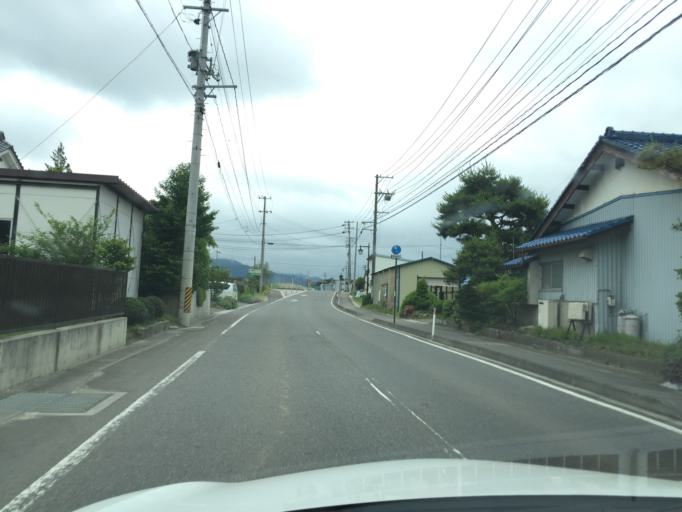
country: JP
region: Fukushima
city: Funehikimachi-funehiki
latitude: 37.4112
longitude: 140.6101
